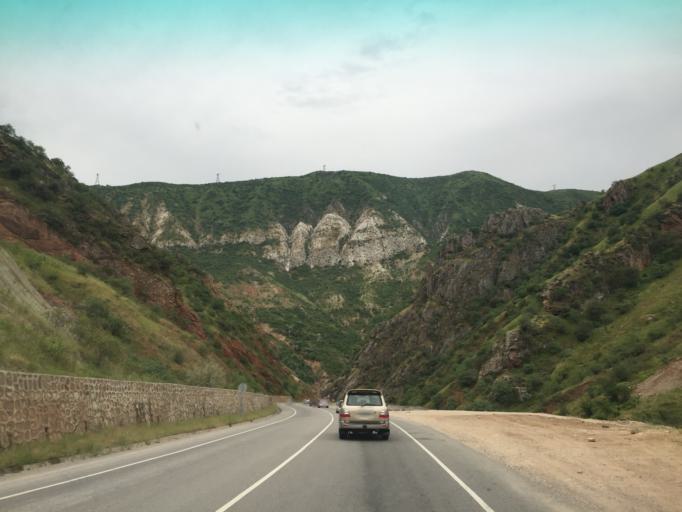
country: TJ
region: Khatlon
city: Norak
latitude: 38.4330
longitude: 69.2086
